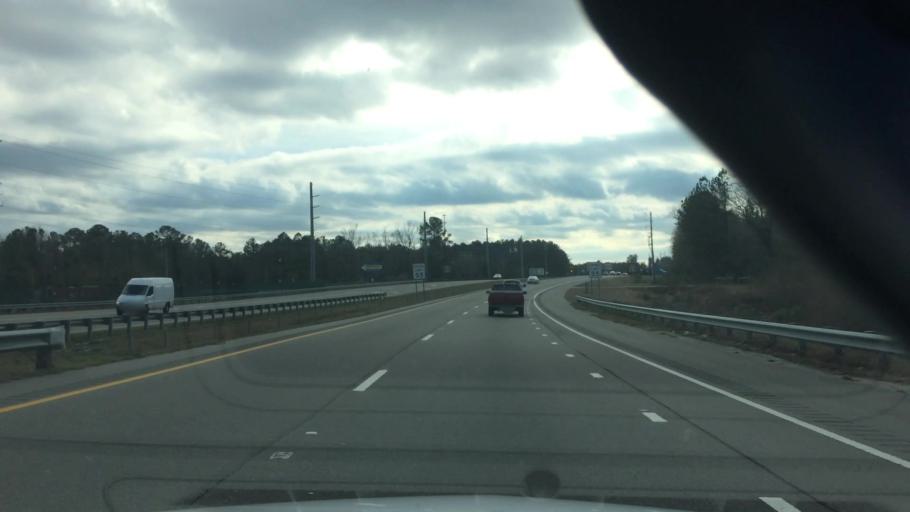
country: US
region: North Carolina
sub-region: Brunswick County
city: Leland
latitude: 34.1827
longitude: -78.0829
